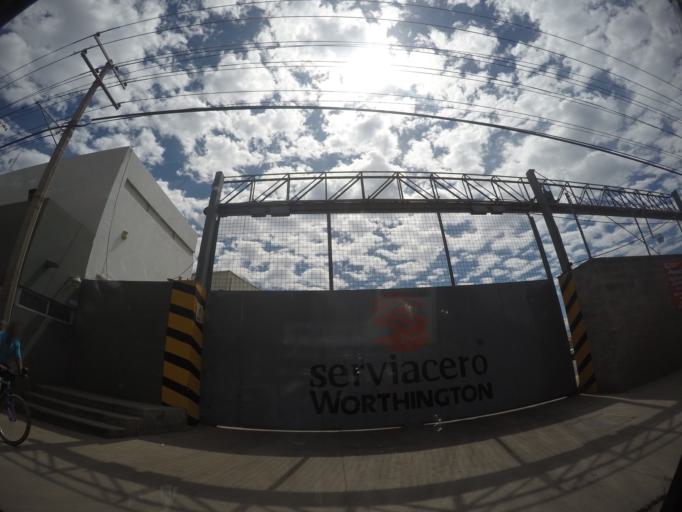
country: MX
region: Guanajuato
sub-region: Leon
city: Santa Ana
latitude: 21.0636
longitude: -101.6853
